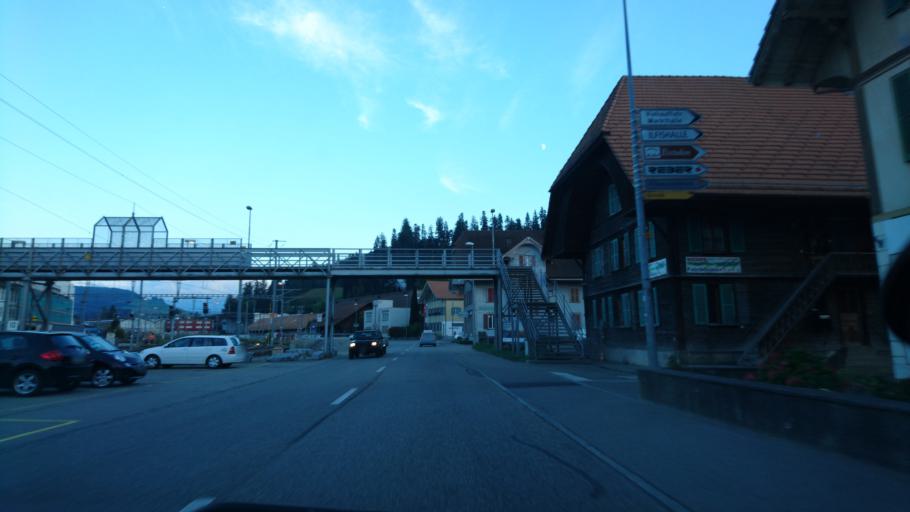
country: CH
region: Bern
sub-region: Emmental District
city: Langnau
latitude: 46.9376
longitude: 7.7859
